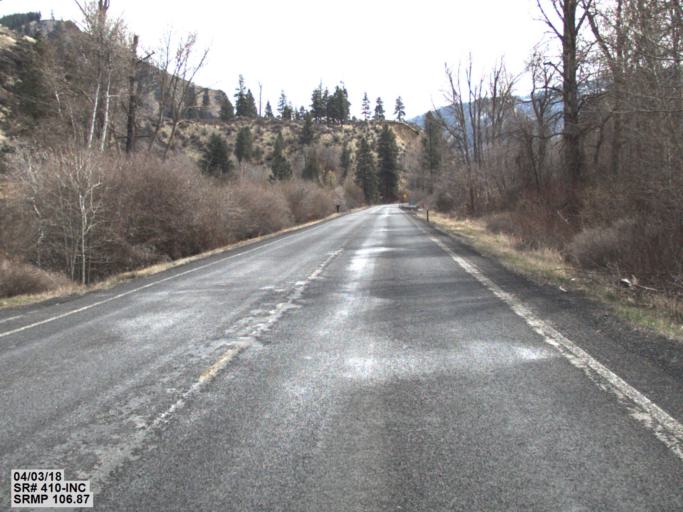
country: US
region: Washington
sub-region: Yakima County
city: Tieton
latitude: 46.8268
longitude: -120.9340
